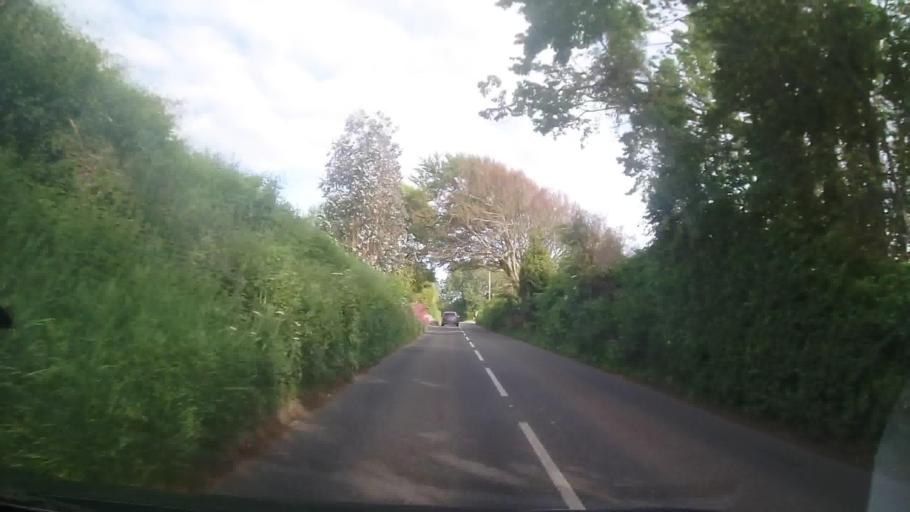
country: GB
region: England
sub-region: Devon
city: Kingsbridge
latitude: 50.2709
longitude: -3.7598
